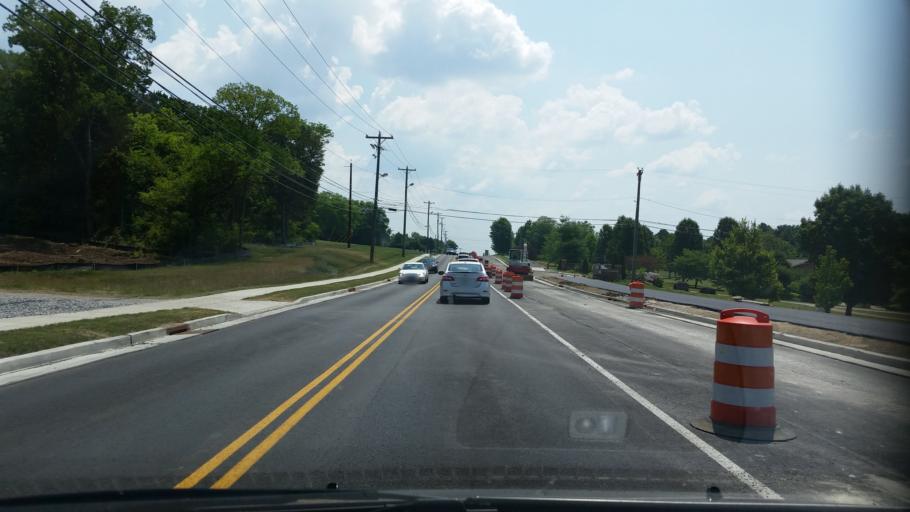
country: US
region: Tennessee
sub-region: Williamson County
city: Brentwood Estates
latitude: 35.9943
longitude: -86.7651
